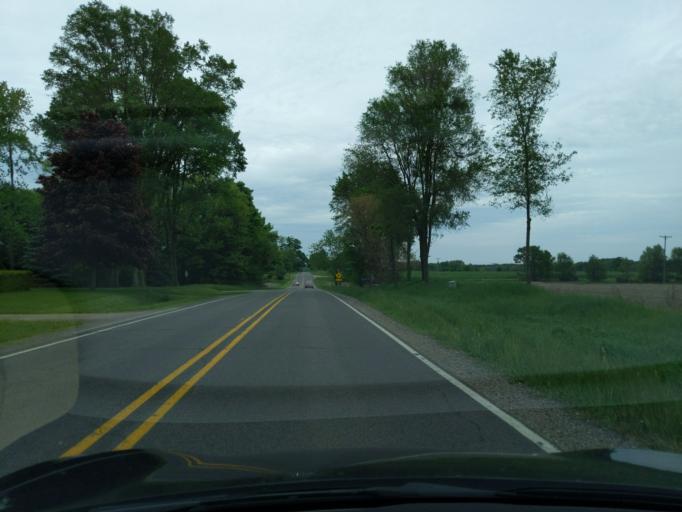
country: US
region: Michigan
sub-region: Ingham County
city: Leslie
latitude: 42.4872
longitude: -84.3562
